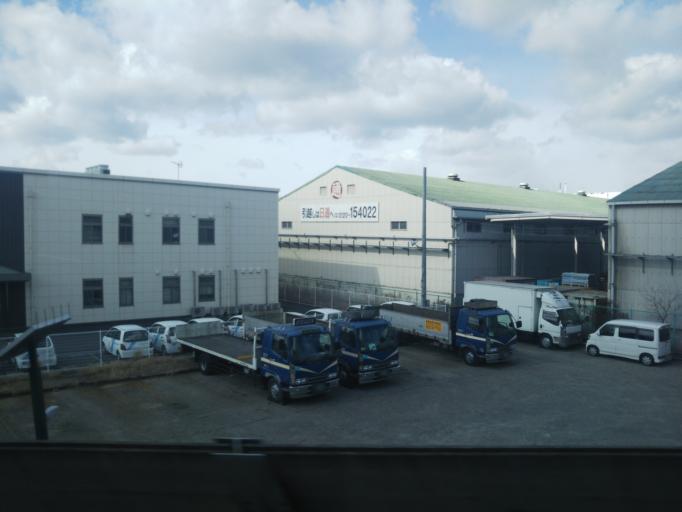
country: JP
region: Okayama
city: Okayama-shi
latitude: 34.6308
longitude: 133.8991
